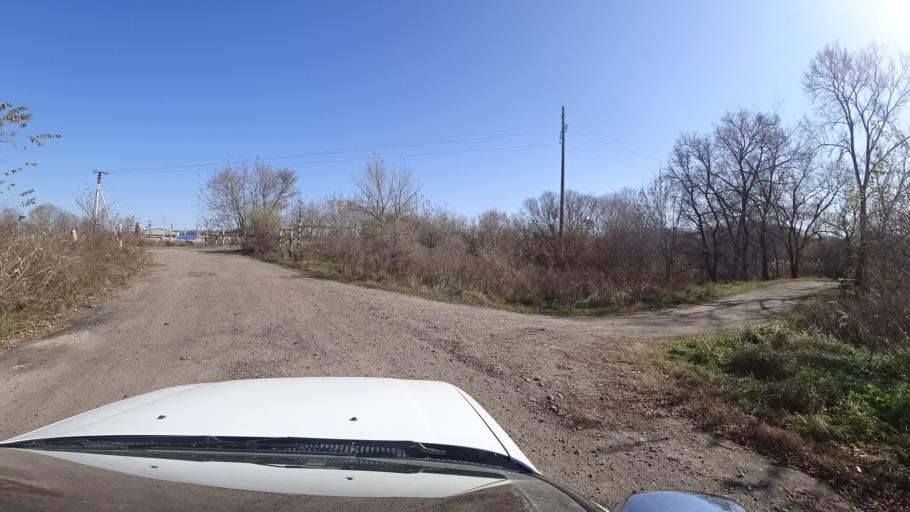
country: RU
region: Primorskiy
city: Dal'nerechensk
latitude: 45.9110
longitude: 133.7957
